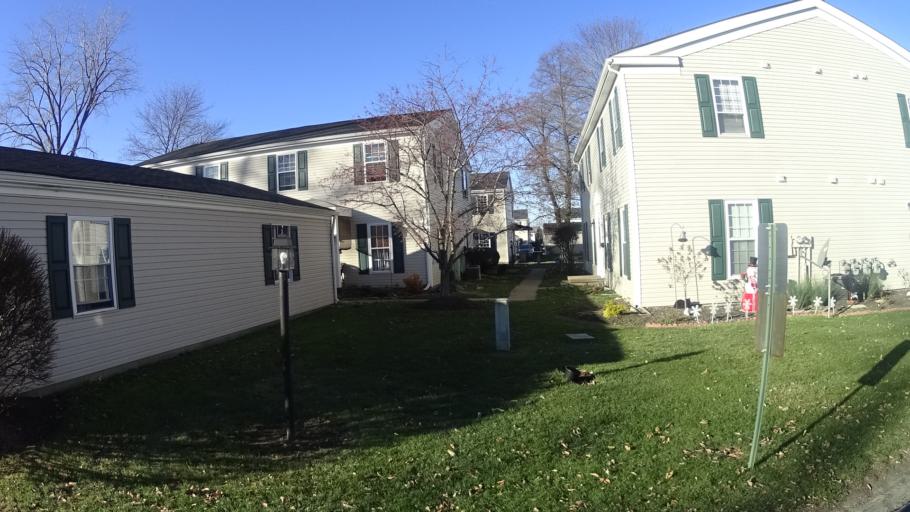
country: US
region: Ohio
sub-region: Lorain County
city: Elyria
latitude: 41.3920
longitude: -82.1061
